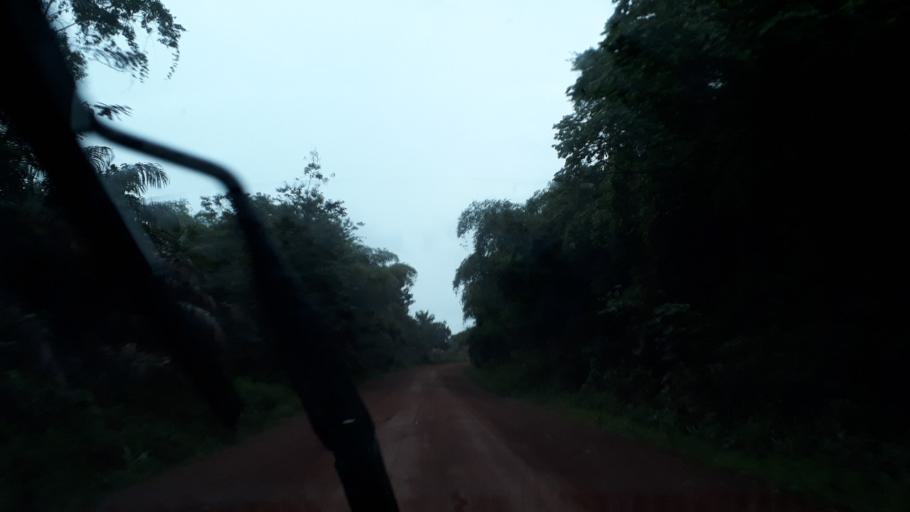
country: CD
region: Eastern Province
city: Kisangani
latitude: 0.4734
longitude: 25.4786
